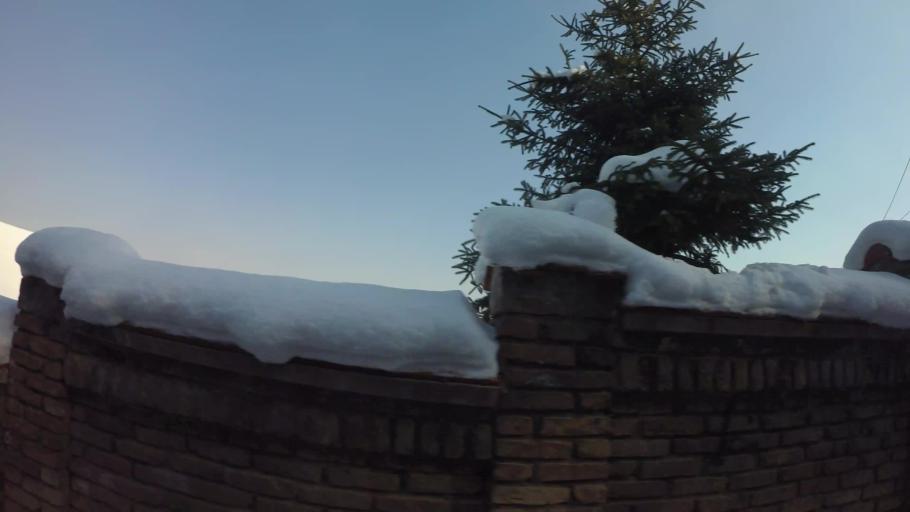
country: BA
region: Federation of Bosnia and Herzegovina
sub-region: Kanton Sarajevo
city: Sarajevo
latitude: 43.8424
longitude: 18.3772
